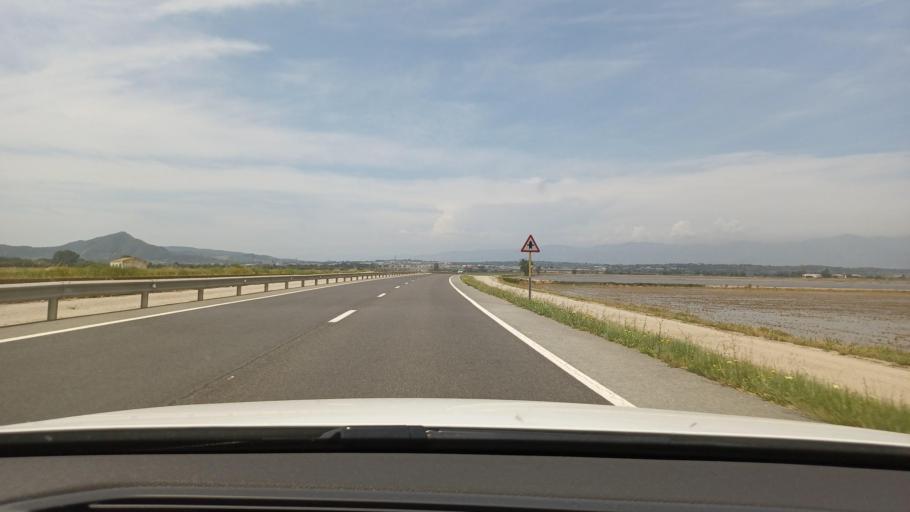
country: ES
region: Catalonia
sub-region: Provincia de Tarragona
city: Amposta
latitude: 40.7123
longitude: 0.6155
